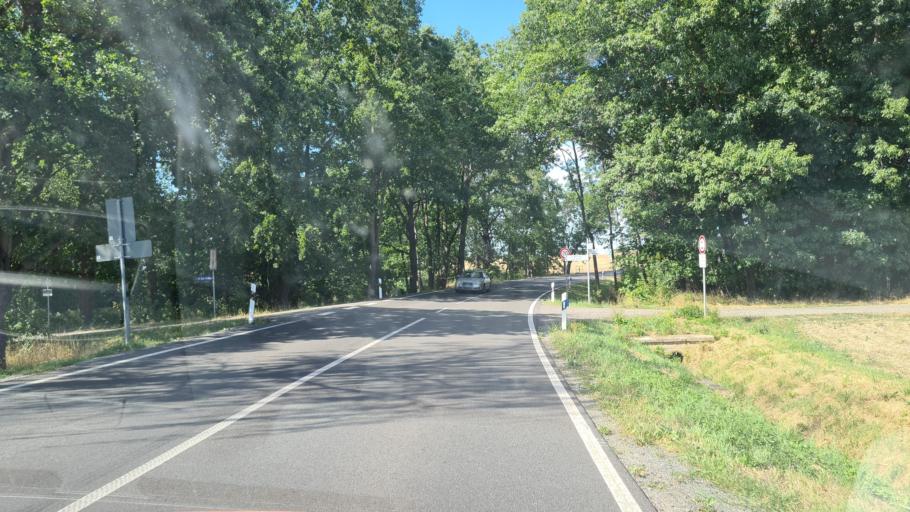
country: DE
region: Saxony
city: Machern
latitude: 51.3830
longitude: 12.6518
